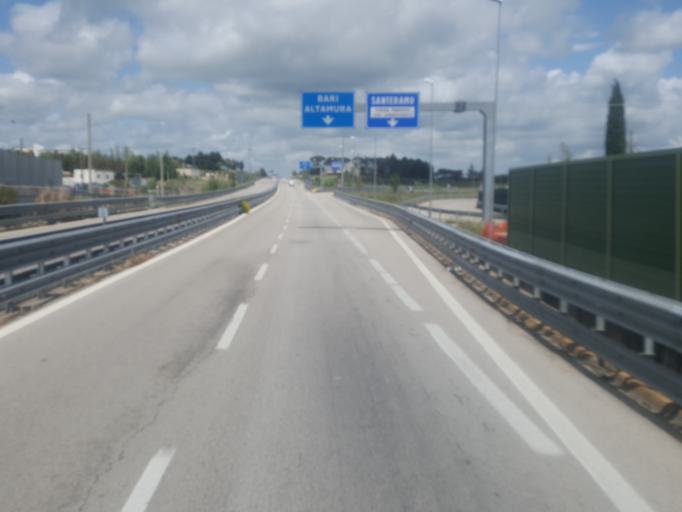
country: IT
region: Basilicate
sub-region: Provincia di Matera
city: Matera
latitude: 40.6967
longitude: 16.5905
